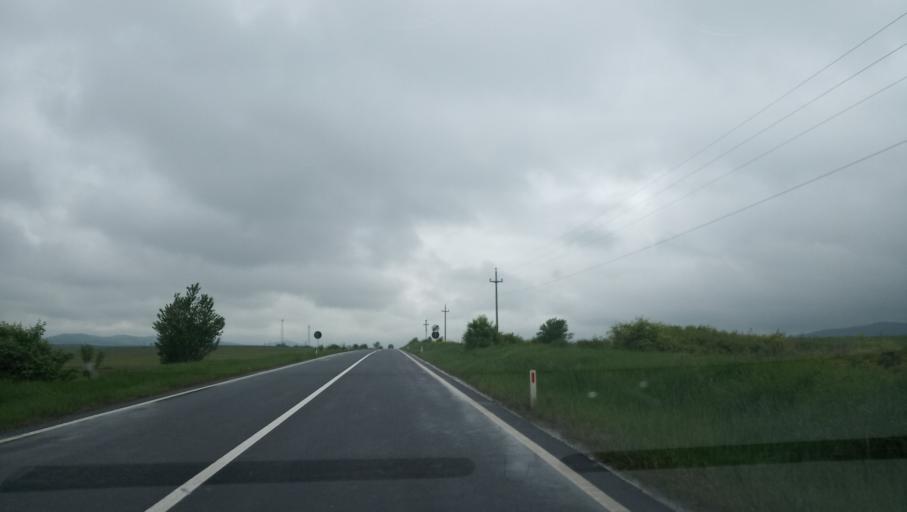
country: RO
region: Alba
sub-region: Comuna Cut
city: Cut
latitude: 45.9199
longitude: 23.6857
